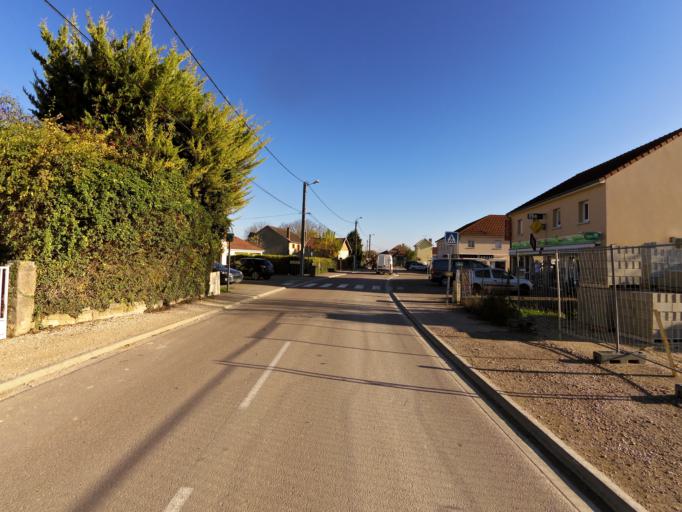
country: FR
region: Champagne-Ardenne
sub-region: Departement de l'Aube
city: Rosieres-pres-Troyes
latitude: 48.2582
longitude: 4.0600
